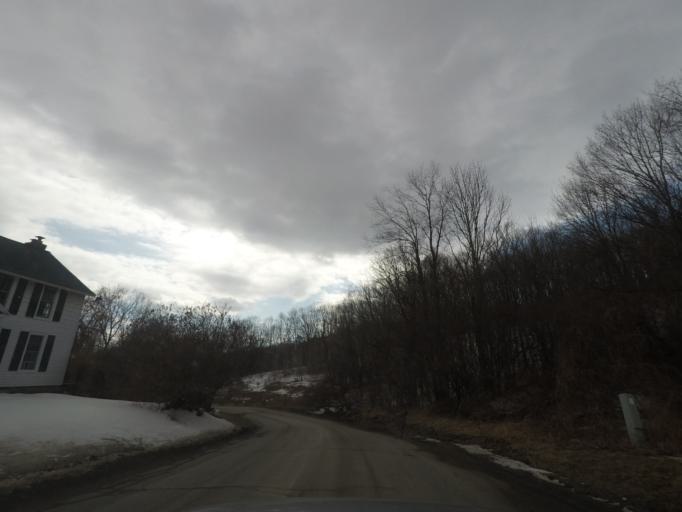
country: US
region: New York
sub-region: Saratoga County
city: Waterford
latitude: 42.7796
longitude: -73.6243
